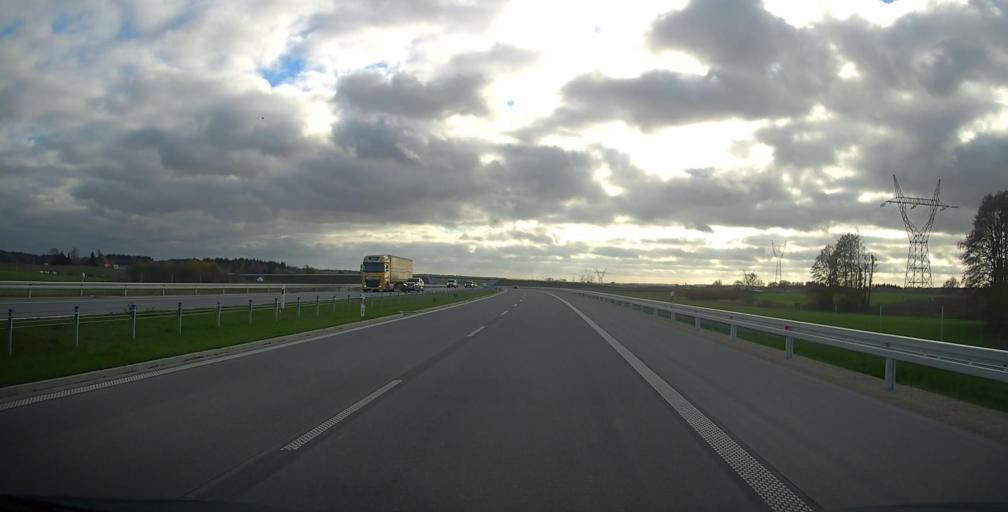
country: PL
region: Podlasie
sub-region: Powiat grajewski
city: Szczuczyn
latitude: 53.6413
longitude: 22.2917
